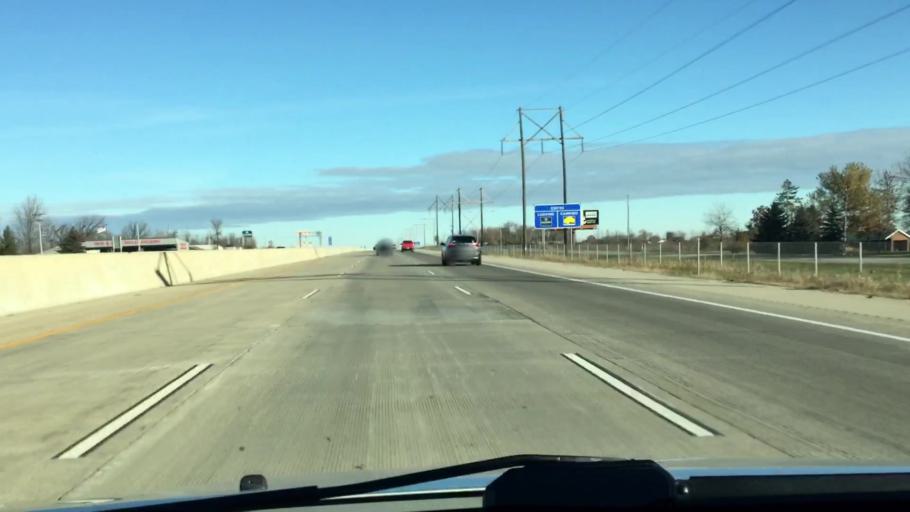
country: US
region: Wisconsin
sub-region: Winnebago County
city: Oshkosh
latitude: 43.9401
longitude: -88.5832
